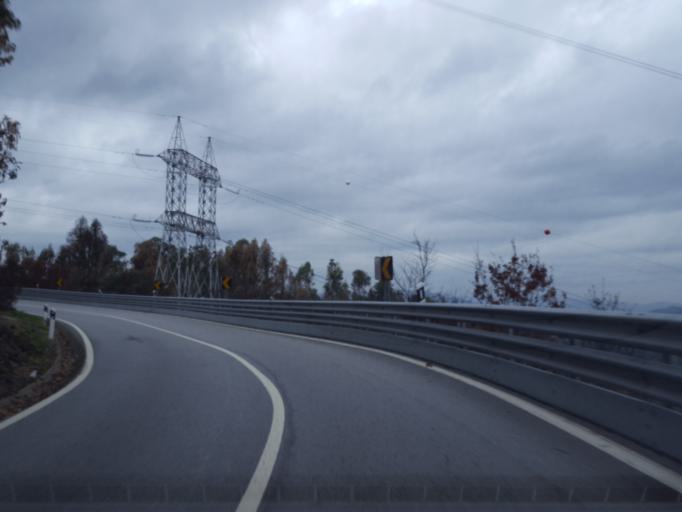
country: PT
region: Porto
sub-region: Marco de Canaveses
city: Marco de Canavezes
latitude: 41.1531
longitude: -8.1335
